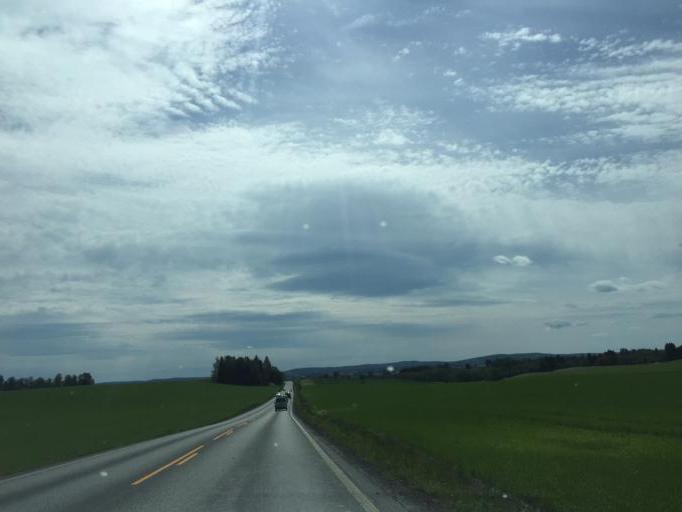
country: NO
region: Akershus
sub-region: Nes
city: Arnes
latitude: 60.1349
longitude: 11.4361
